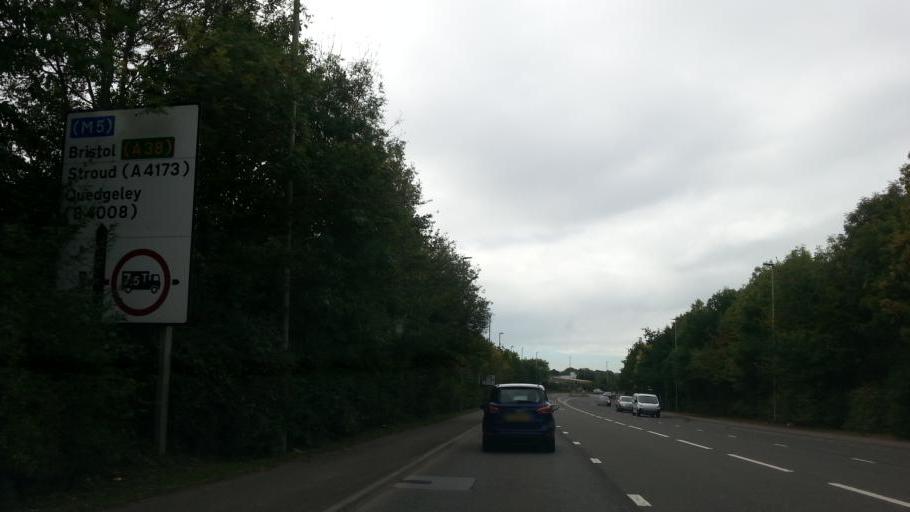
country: GB
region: England
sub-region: Gloucestershire
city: Gloucester
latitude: 51.8483
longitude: -2.2640
